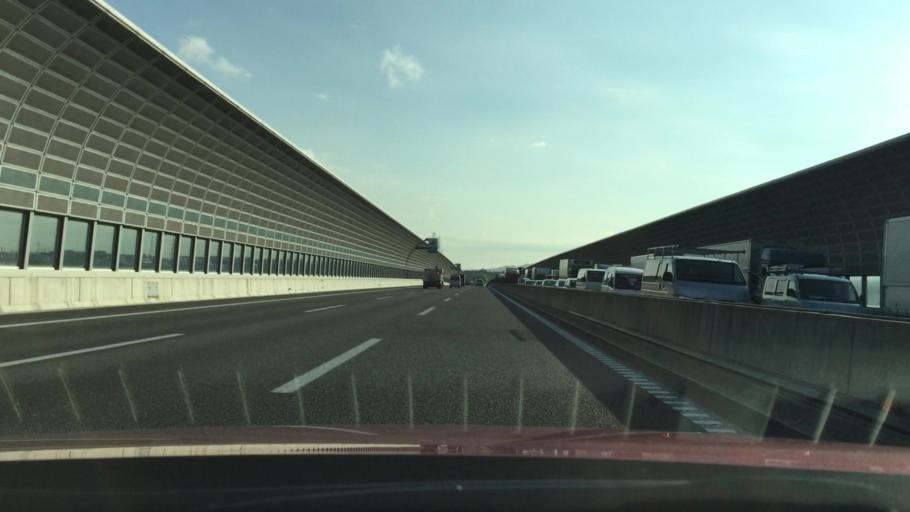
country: JP
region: Osaka
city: Neyagawa
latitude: 34.7491
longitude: 135.6304
